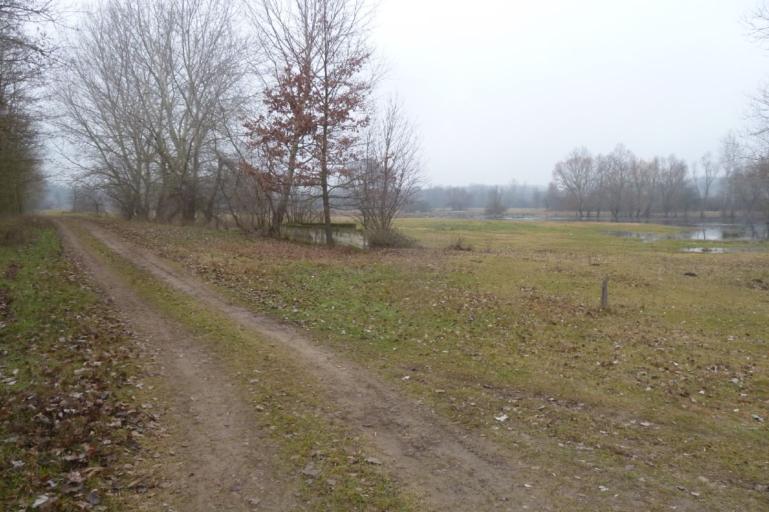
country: HU
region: Pest
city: Tapiosag
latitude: 47.4221
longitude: 19.6412
